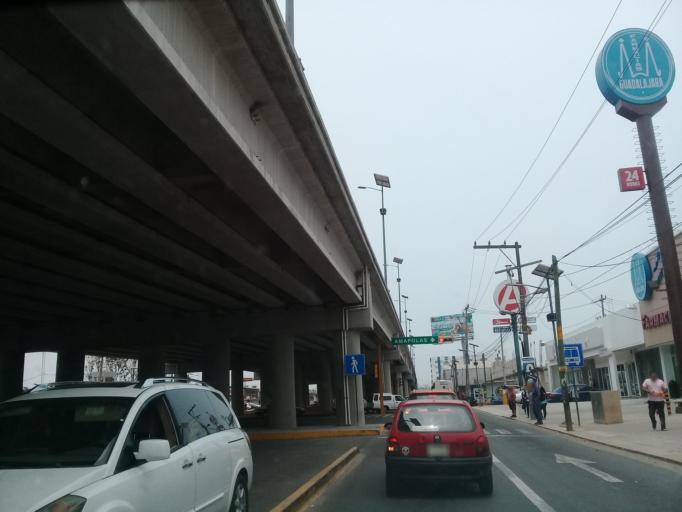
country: MX
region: Veracruz
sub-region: Veracruz
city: Las Amapolas
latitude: 19.1582
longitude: -96.1965
